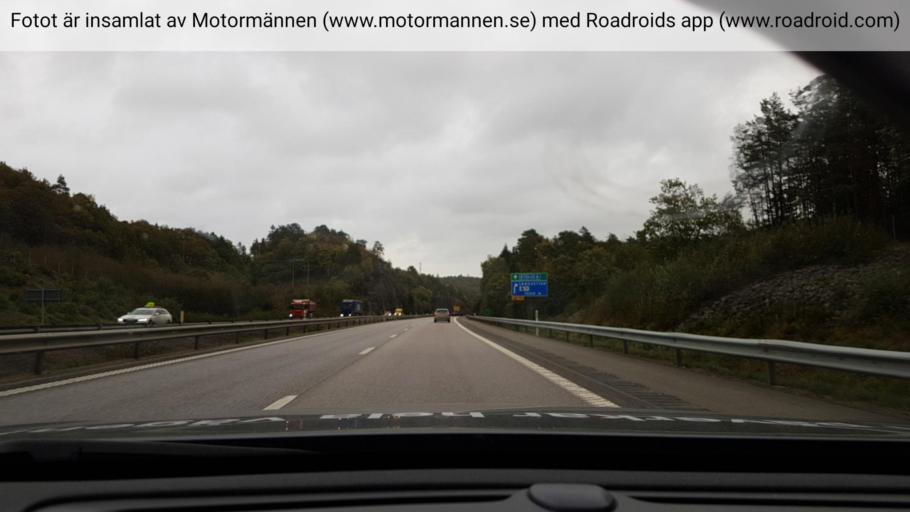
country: SE
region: Vaestra Goetaland
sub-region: Harryda Kommun
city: Landvetter
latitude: 57.6850
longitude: 12.1813
